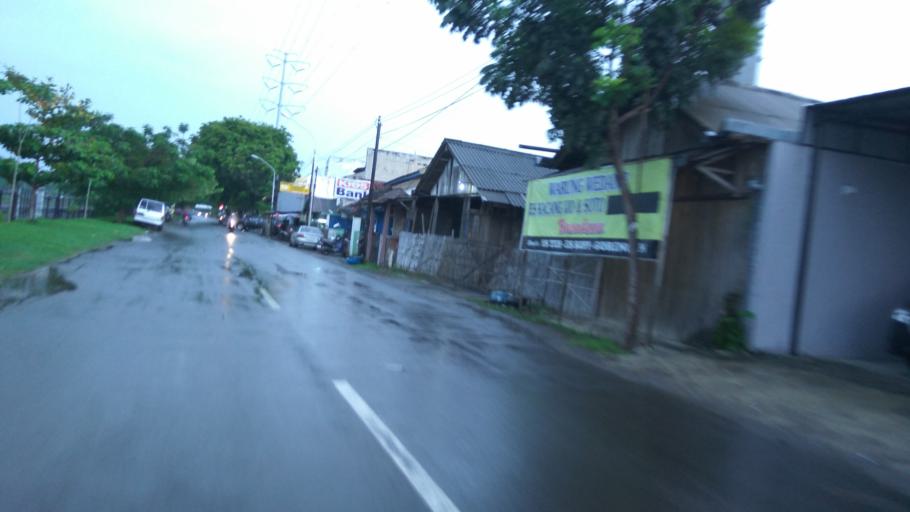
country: ID
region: Central Java
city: Semarang
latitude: -6.9884
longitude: 110.4029
